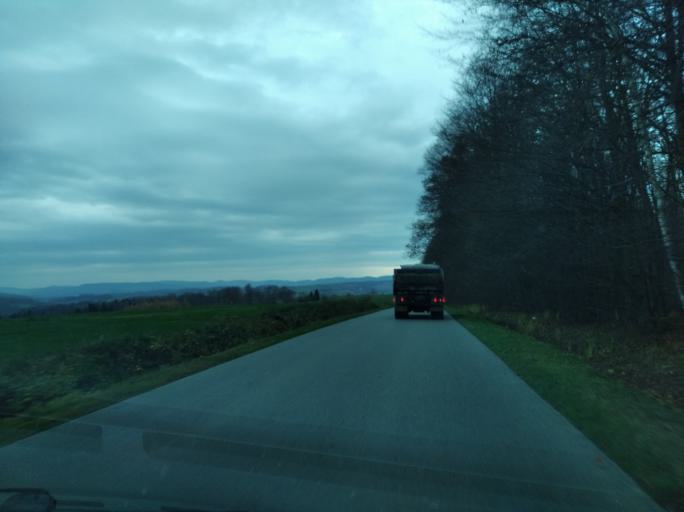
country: PL
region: Subcarpathian Voivodeship
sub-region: Powiat ropczycko-sedziszowski
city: Zagorzyce
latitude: 49.9455
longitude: 21.6939
